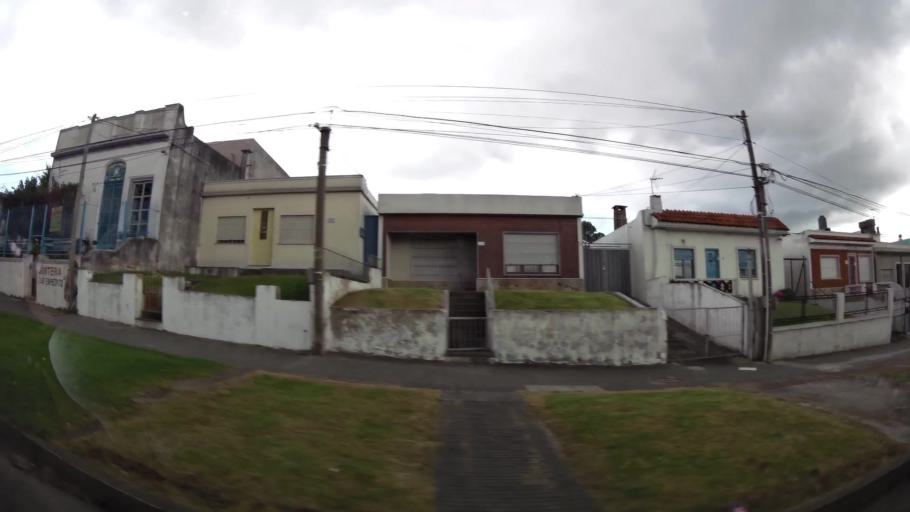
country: UY
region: Montevideo
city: Montevideo
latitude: -34.8496
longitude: -56.1705
